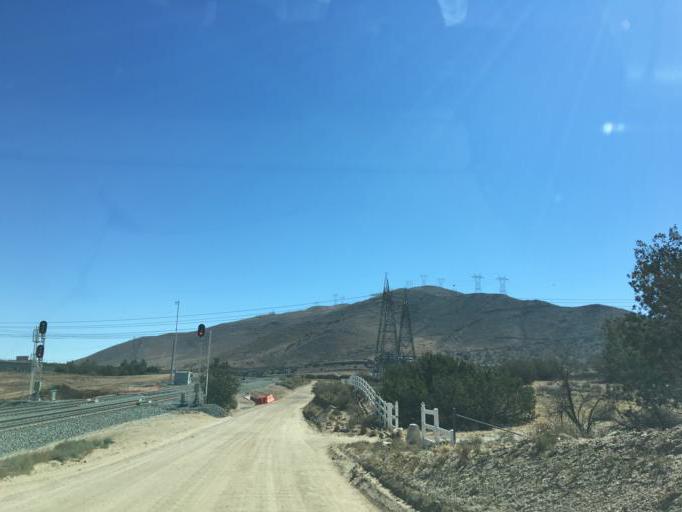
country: US
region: California
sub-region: Los Angeles County
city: Vincent
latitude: 34.4939
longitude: -118.1234
